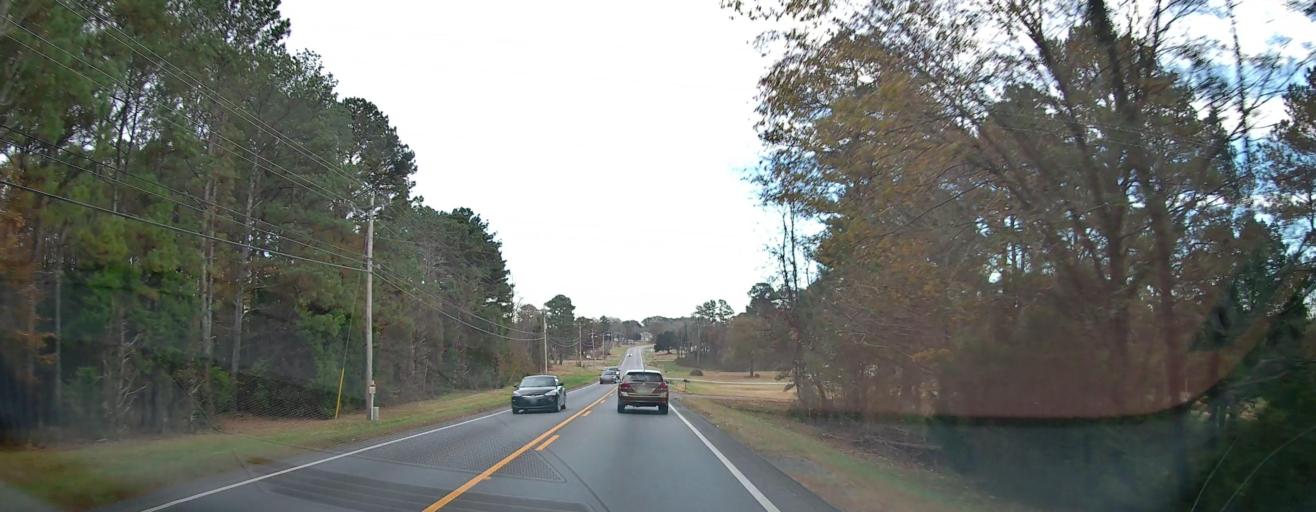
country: US
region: Alabama
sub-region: Morgan County
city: Priceville
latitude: 34.5039
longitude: -86.8631
